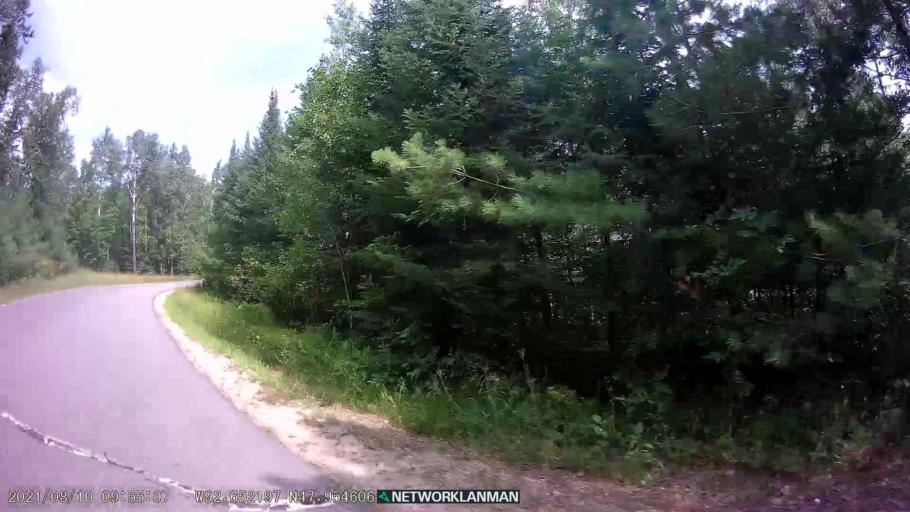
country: US
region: Minnesota
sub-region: Saint Louis County
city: Mountain Iron
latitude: 47.9548
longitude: -92.6527
